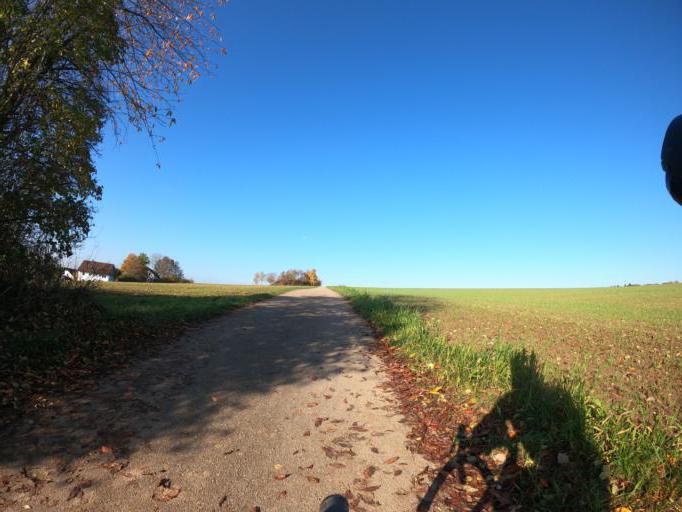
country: DE
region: Baden-Wuerttemberg
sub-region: Regierungsbezirk Stuttgart
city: Aidlingen
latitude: 48.7205
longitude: 8.9102
